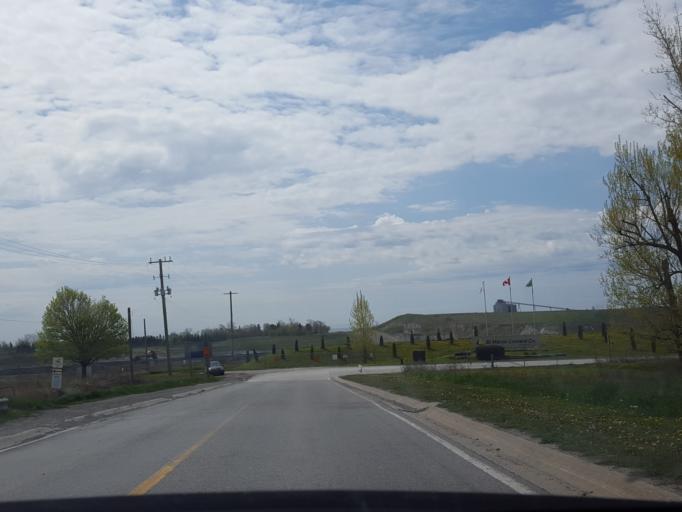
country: CA
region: Ontario
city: Oshawa
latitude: 43.8919
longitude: -78.6882
